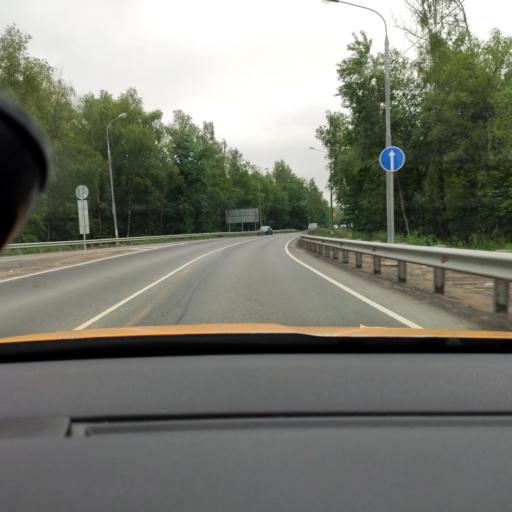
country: RU
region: Moskovskaya
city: Danki
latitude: 54.9200
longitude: 37.5102
